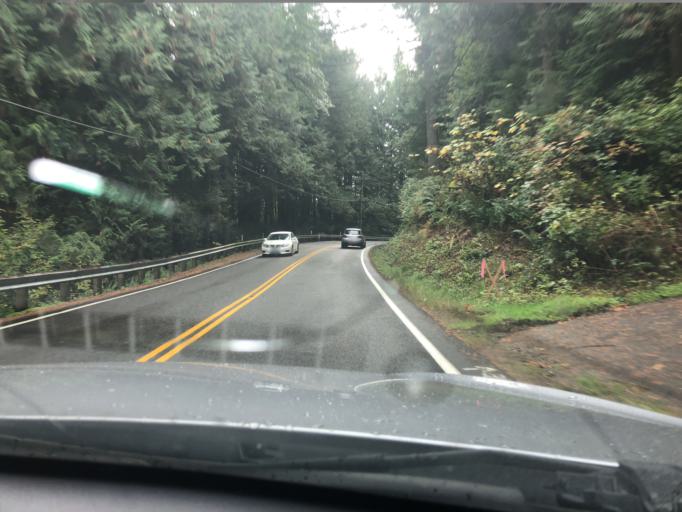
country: US
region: Washington
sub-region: King County
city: Riverbend
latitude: 47.4594
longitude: -121.7573
